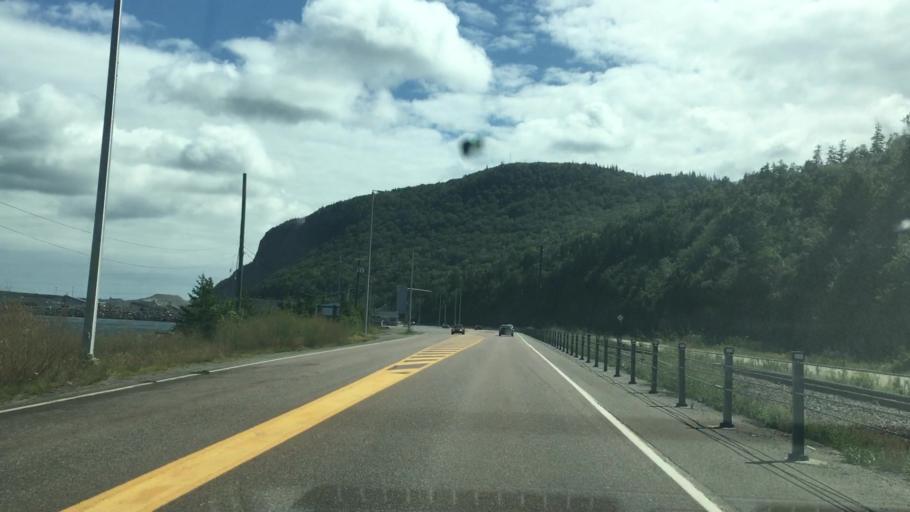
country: CA
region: Nova Scotia
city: Port Hawkesbury
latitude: 45.6434
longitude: -61.4319
